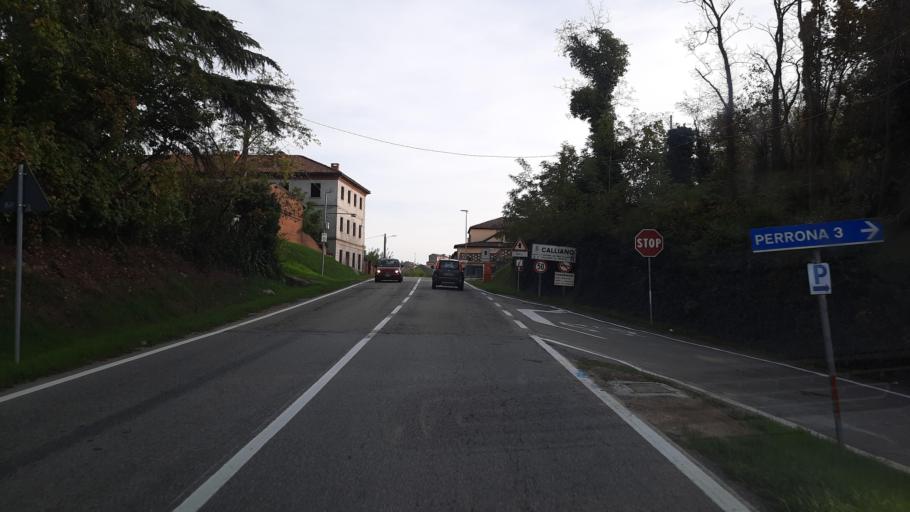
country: IT
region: Piedmont
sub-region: Provincia di Asti
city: Calliano
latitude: 45.0124
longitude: 8.2548
